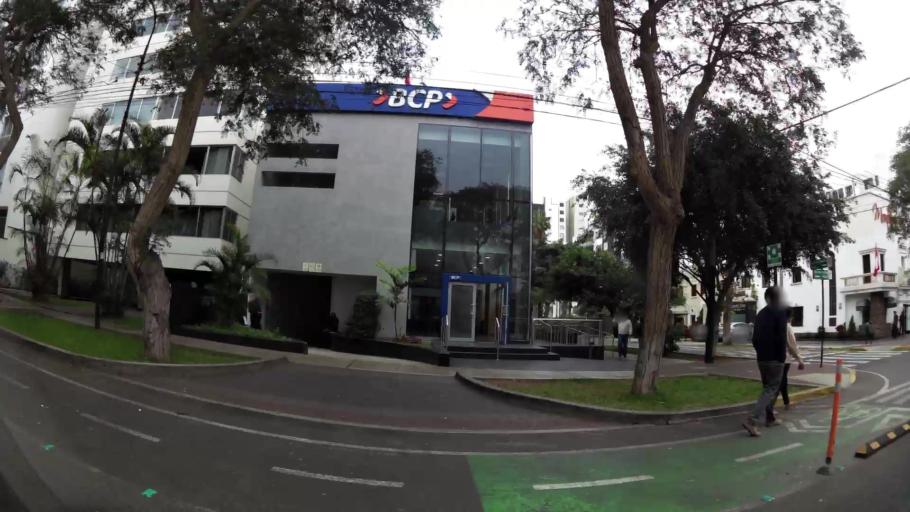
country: PE
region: Lima
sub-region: Lima
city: San Isidro
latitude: -12.0919
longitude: -77.0429
